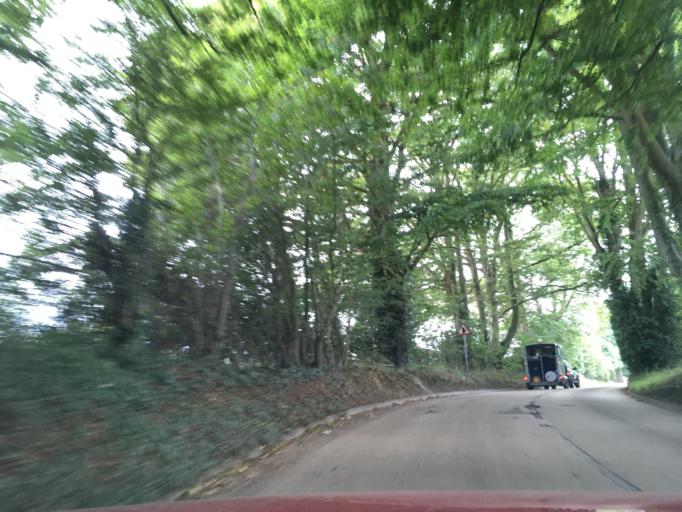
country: GB
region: England
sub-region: Kent
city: Yalding
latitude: 51.2367
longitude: 0.4461
